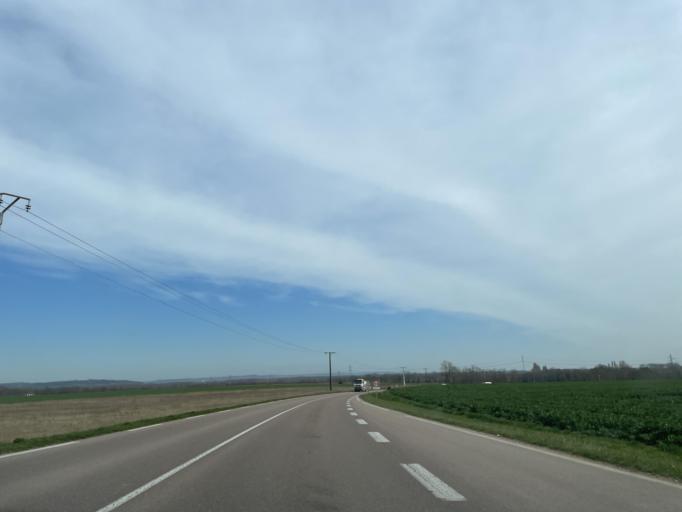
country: FR
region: Champagne-Ardenne
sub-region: Departement de l'Aube
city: Nogent-sur-Seine
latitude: 48.4923
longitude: 3.5220
